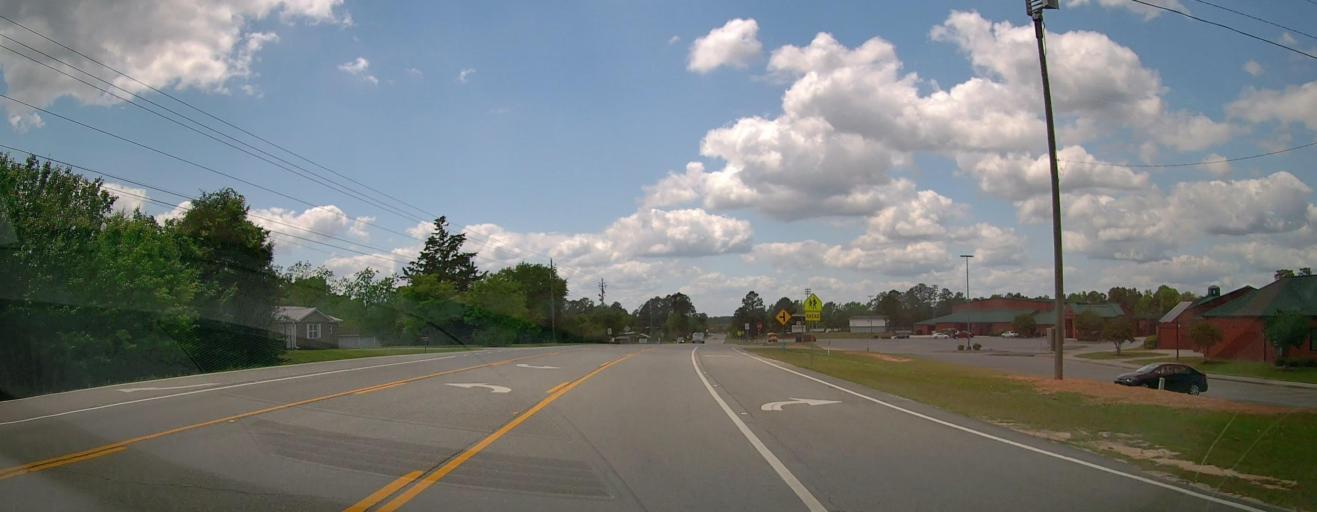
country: US
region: Georgia
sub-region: Laurens County
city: East Dublin
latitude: 32.5610
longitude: -82.8179
